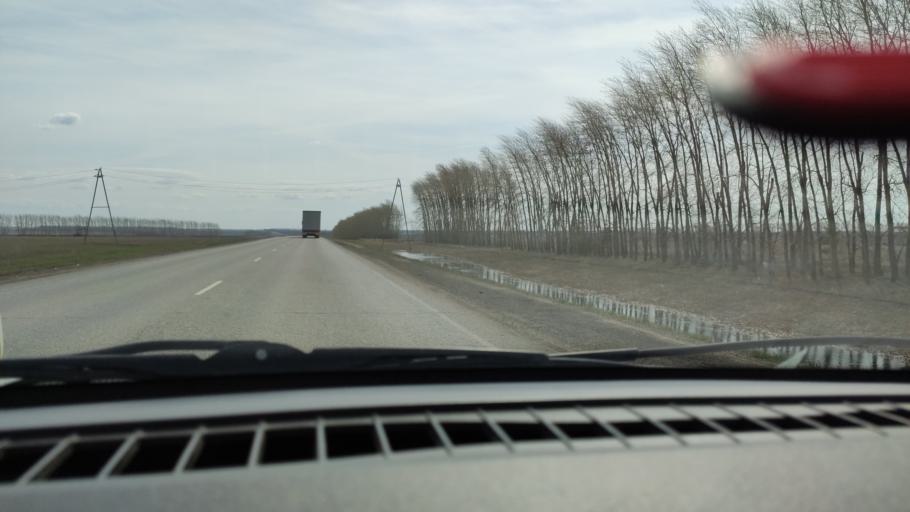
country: RU
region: Bashkortostan
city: Dyurtyuli
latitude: 55.3715
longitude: 54.8802
